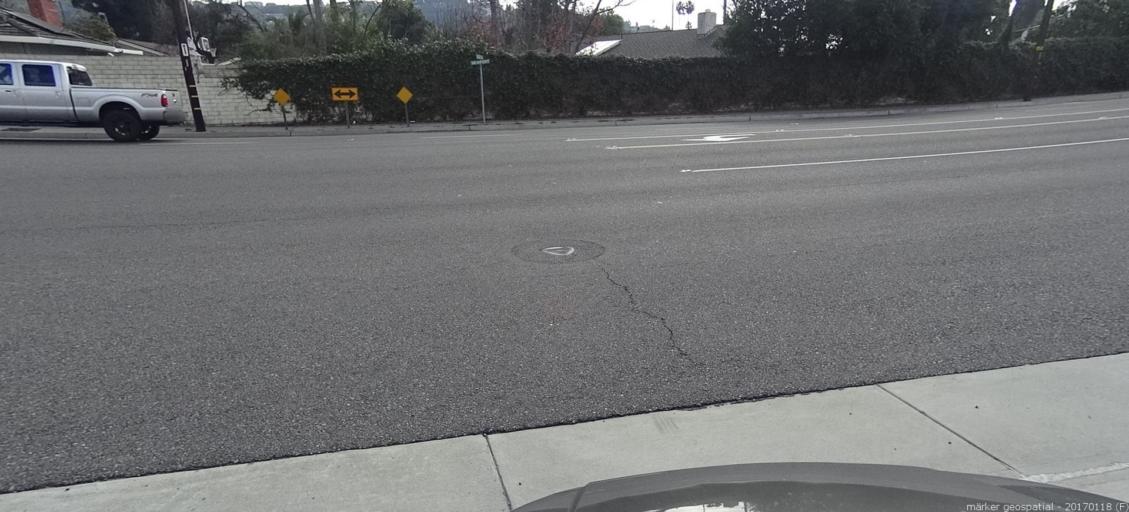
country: US
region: California
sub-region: Orange County
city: North Tustin
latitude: 33.7695
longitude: -117.7932
